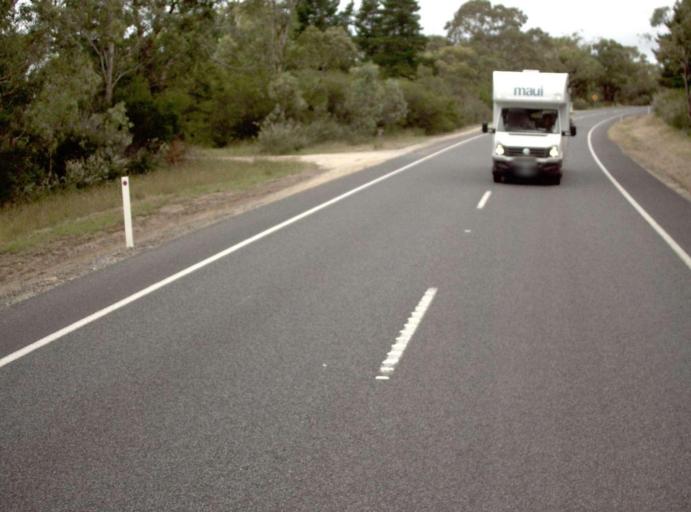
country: AU
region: Victoria
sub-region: Wellington
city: Sale
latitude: -38.1959
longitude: 147.0782
